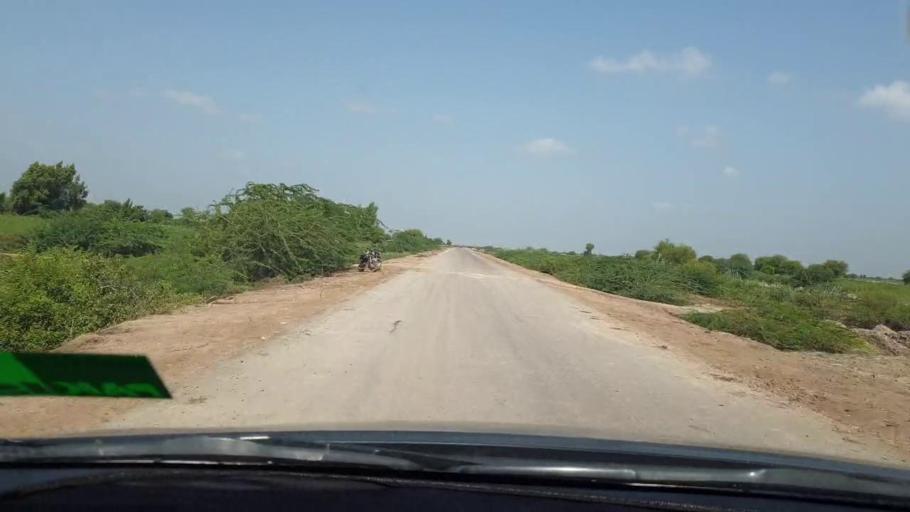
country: PK
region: Sindh
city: Digri
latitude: 24.9833
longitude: 69.1274
